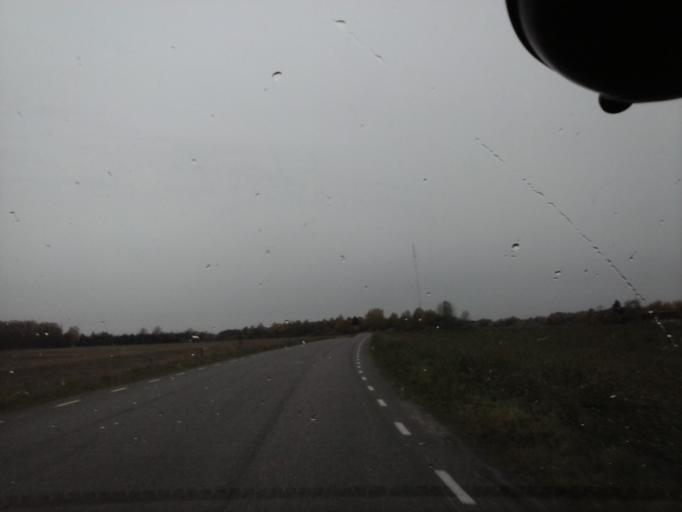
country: EE
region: Viljandimaa
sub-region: Vohma linn
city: Vohma
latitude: 58.6879
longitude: 25.6562
